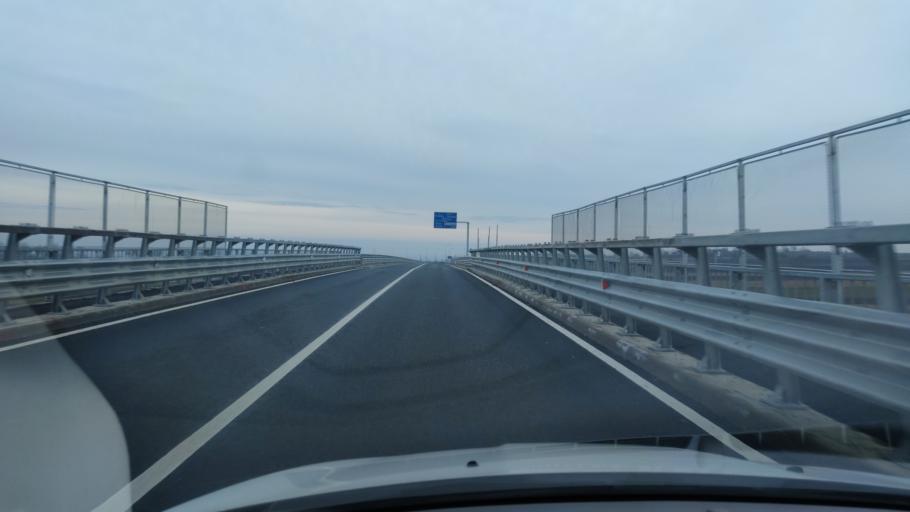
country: RO
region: Bihor
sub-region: Comuna Cherechiu
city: Cherechiu
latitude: 47.3726
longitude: 22.1351
